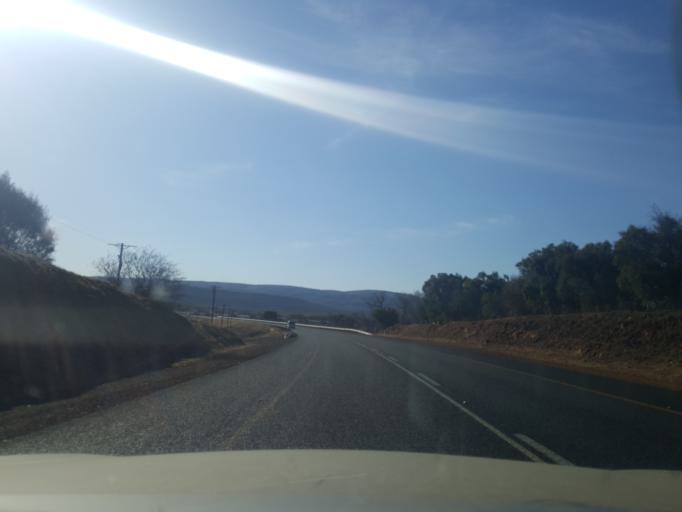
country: ZA
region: North-West
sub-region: Ngaka Modiri Molema District Municipality
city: Zeerust
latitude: -25.5540
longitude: 26.0580
